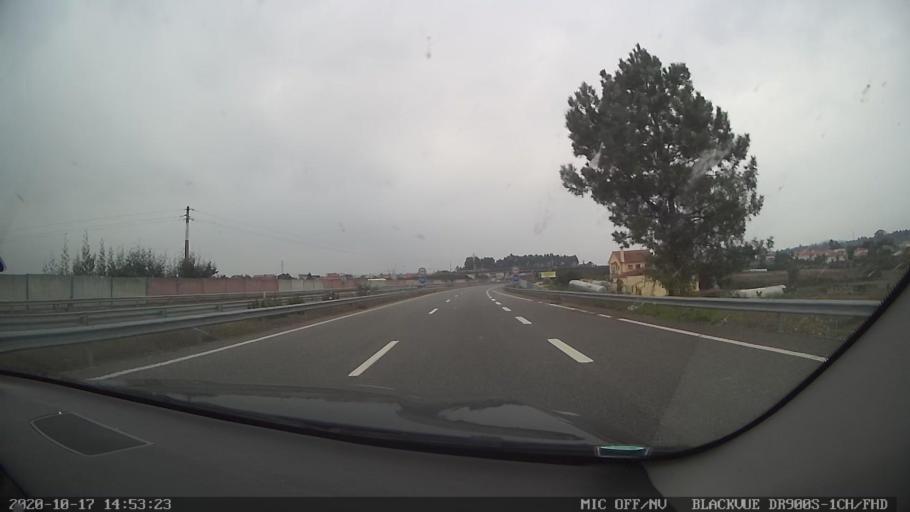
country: PT
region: Braga
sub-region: Barcelos
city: Vila Frescainha
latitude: 41.5005
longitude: -8.6617
